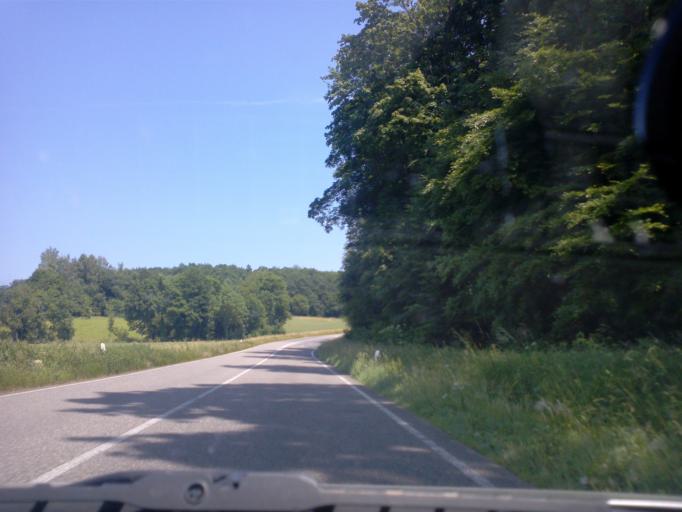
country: DE
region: Baden-Wuerttemberg
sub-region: Karlsruhe Region
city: Joehlingen
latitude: 49.0222
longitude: 8.5542
